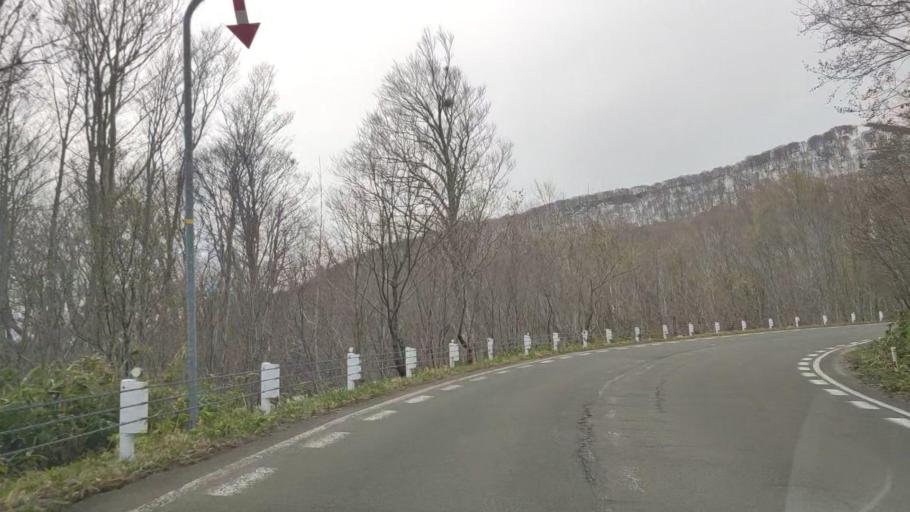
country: JP
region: Aomori
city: Aomori Shi
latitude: 40.6577
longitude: 140.9591
